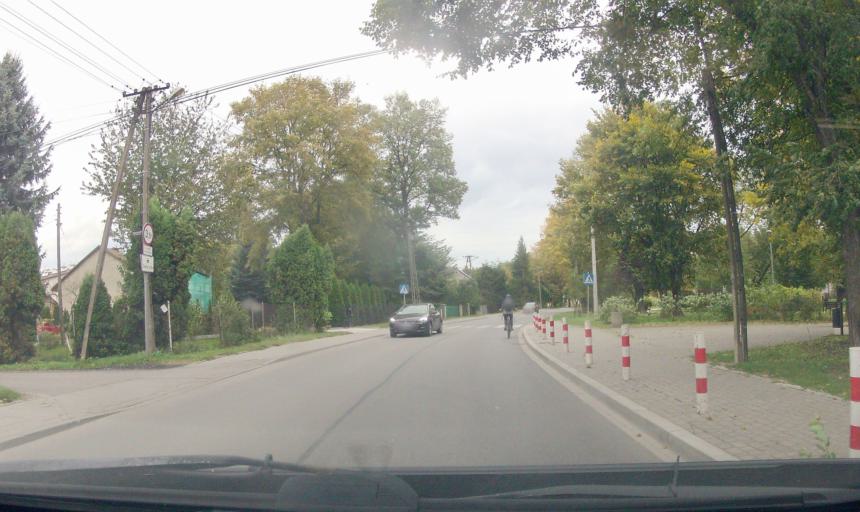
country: PL
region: Lesser Poland Voivodeship
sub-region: Krakow
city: Krakow
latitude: 50.0461
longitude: 19.9883
